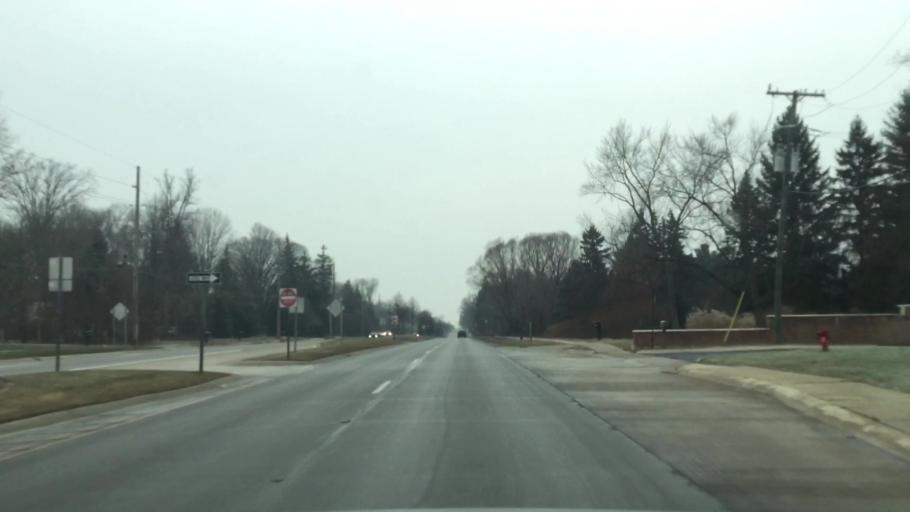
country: US
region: Michigan
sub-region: Oakland County
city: Farmington
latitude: 42.4735
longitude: -83.3574
